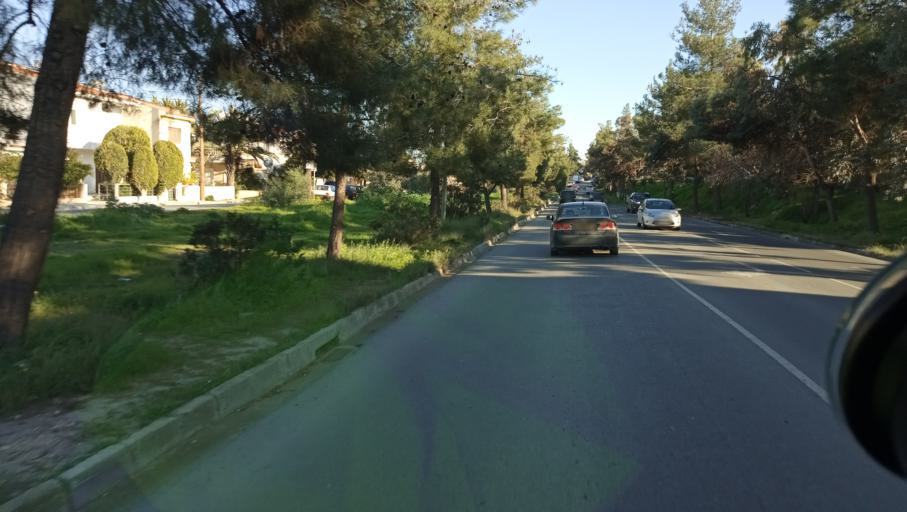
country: CY
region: Lefkosia
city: Kato Deftera
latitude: 35.1404
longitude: 33.3059
